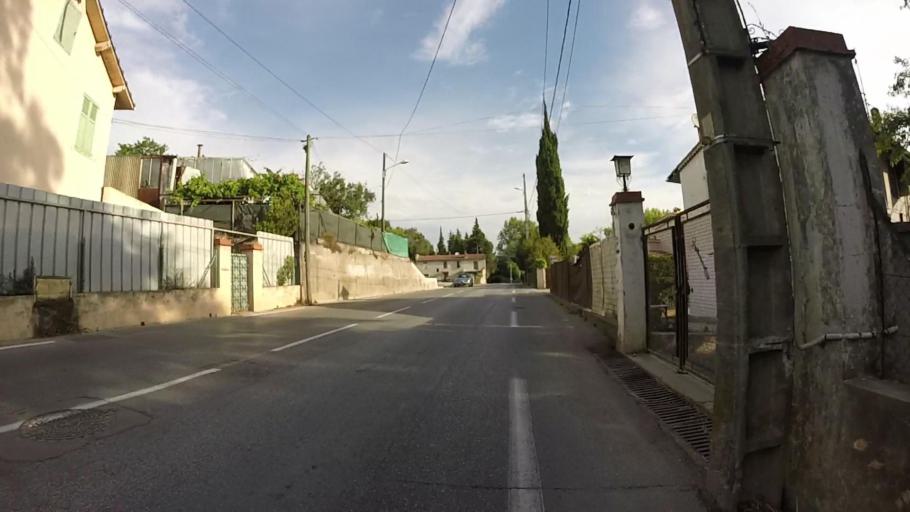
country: FR
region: Provence-Alpes-Cote d'Azur
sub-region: Departement des Alpes-Maritimes
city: Biot
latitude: 43.6096
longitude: 7.1102
